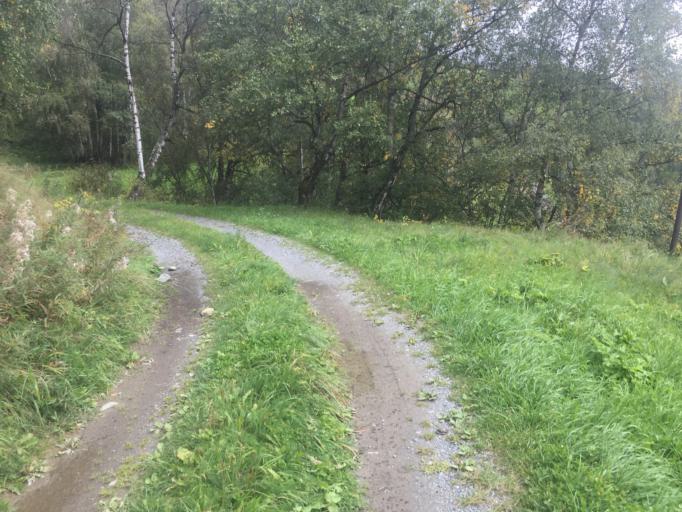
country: CH
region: Grisons
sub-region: Inn District
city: Zernez
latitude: 46.7719
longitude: 10.1293
